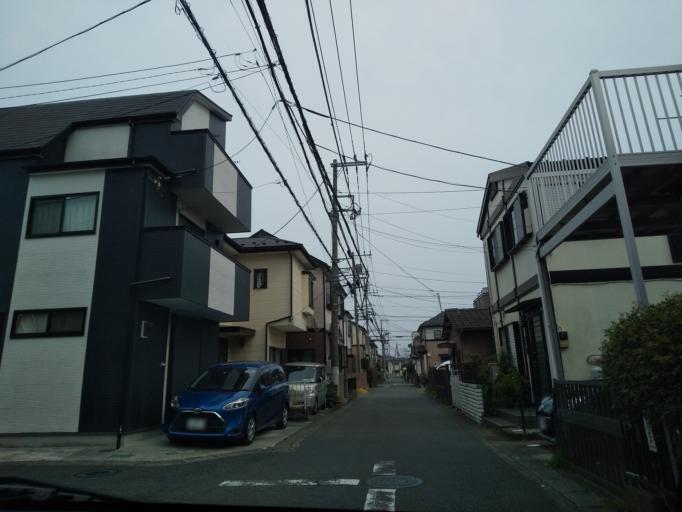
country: JP
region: Kanagawa
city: Minami-rinkan
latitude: 35.4646
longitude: 139.4264
